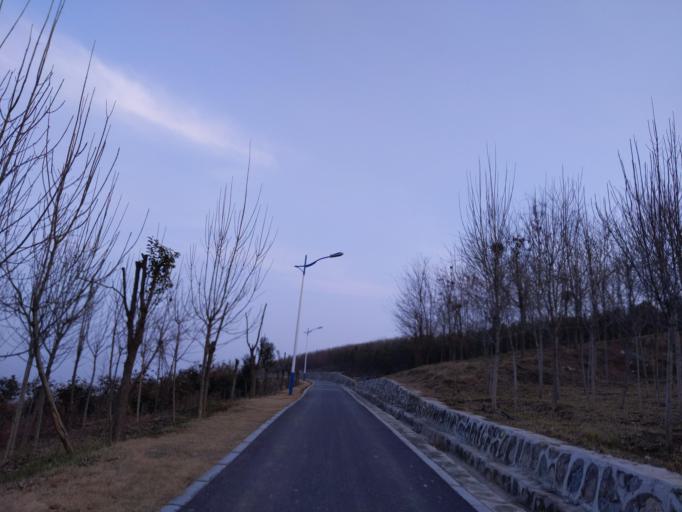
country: CN
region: Henan Sheng
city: Zhongyuanlu
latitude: 35.8177
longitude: 115.0533
